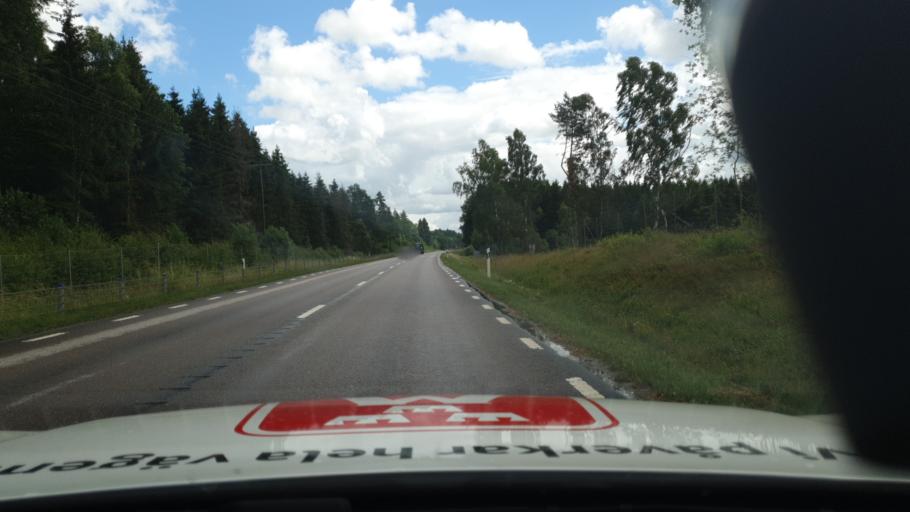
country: SE
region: Vaestra Goetaland
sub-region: Falkopings Kommun
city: Floby
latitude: 58.1776
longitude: 13.3866
